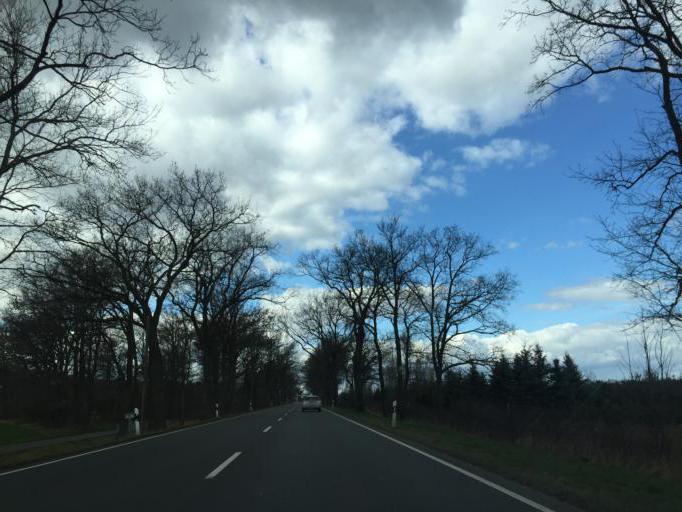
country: DE
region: Lower Saxony
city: Broeckel
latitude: 52.4957
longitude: 10.2376
